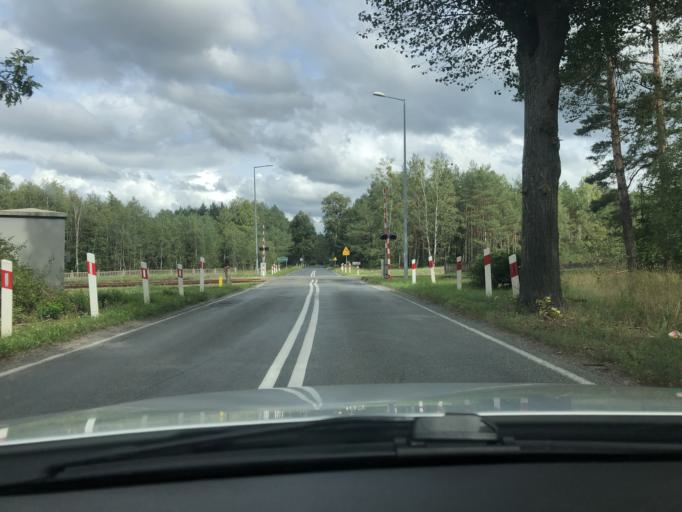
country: PL
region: Greater Poland Voivodeship
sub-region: Powiat czarnkowsko-trzcianecki
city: Krzyz Wielkopolski
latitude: 52.8532
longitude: 15.9242
